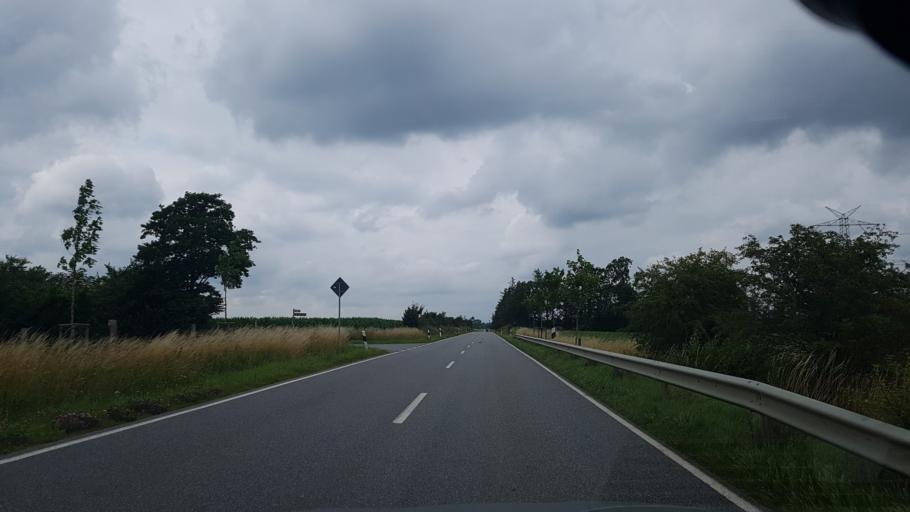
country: DE
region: Schleswig-Holstein
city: Osterby
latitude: 54.8065
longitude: 9.2384
